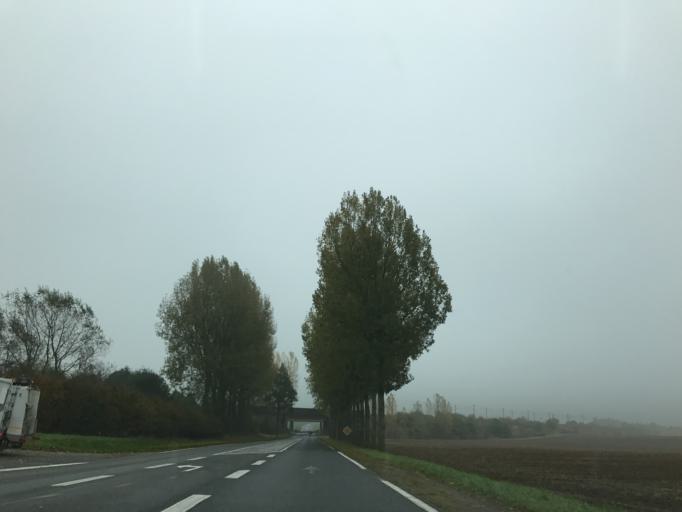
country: FR
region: Nord-Pas-de-Calais
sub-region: Departement du Pas-de-Calais
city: Bapaume
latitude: 50.0900
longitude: 2.8680
